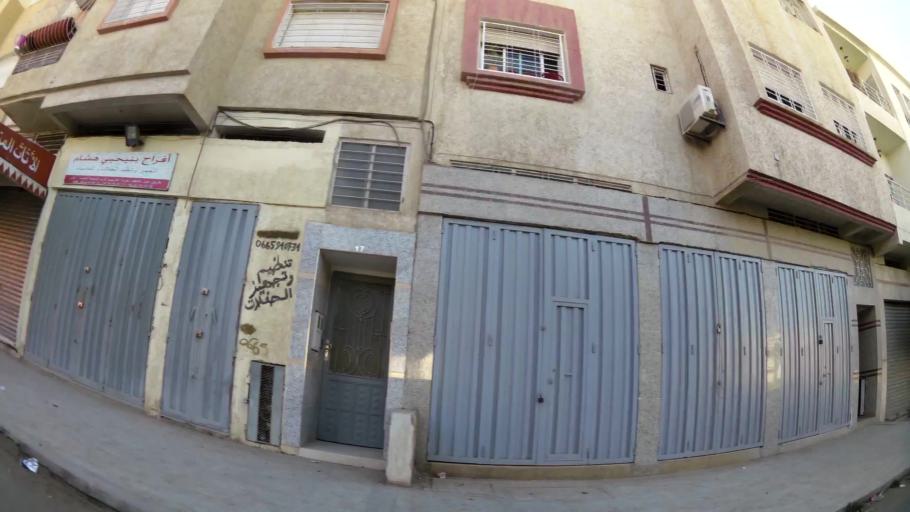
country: MA
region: Fes-Boulemane
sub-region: Fes
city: Fes
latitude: 34.0094
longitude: -5.0161
